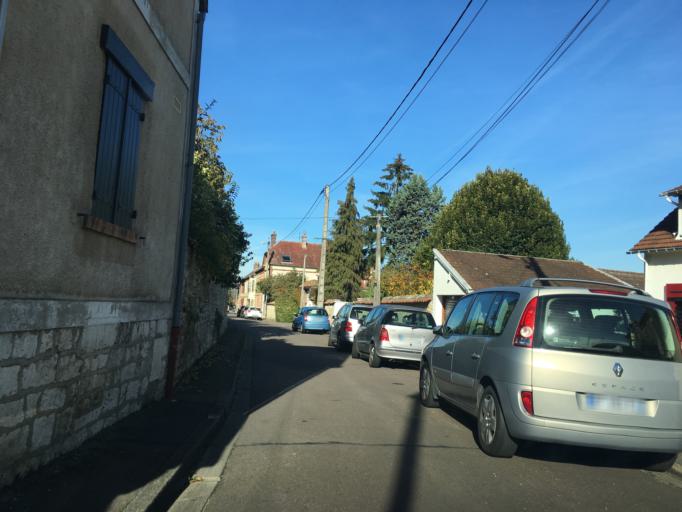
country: FR
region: Haute-Normandie
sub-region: Departement de l'Eure
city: Vernon
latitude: 49.0903
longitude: 1.4580
